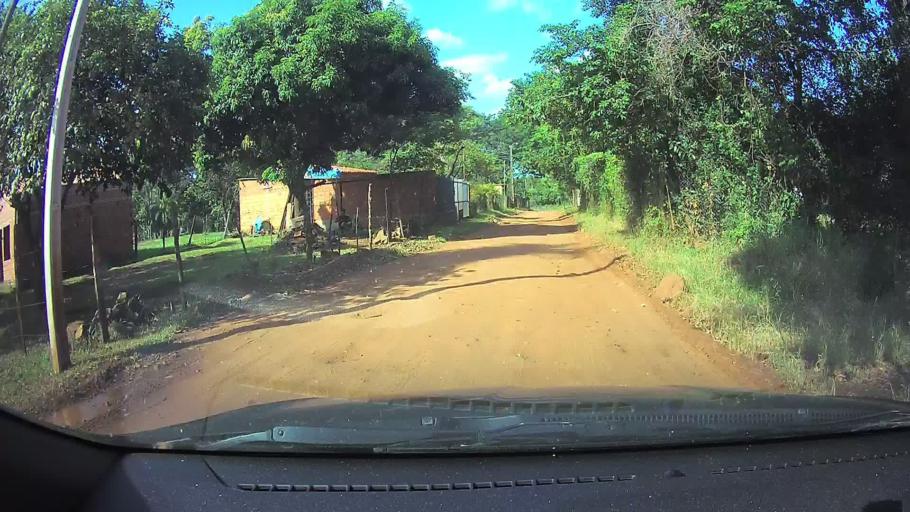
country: PY
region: Central
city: Limpio
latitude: -25.2404
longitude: -57.4649
